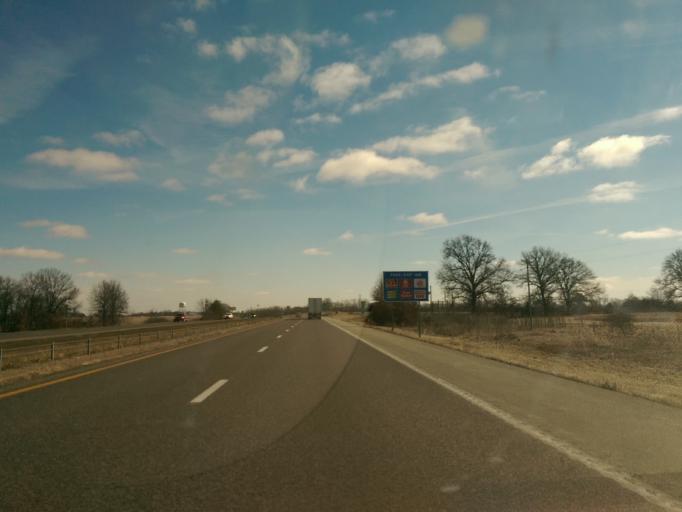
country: US
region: Missouri
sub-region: Callaway County
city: Fulton
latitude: 38.9477
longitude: -91.9572
